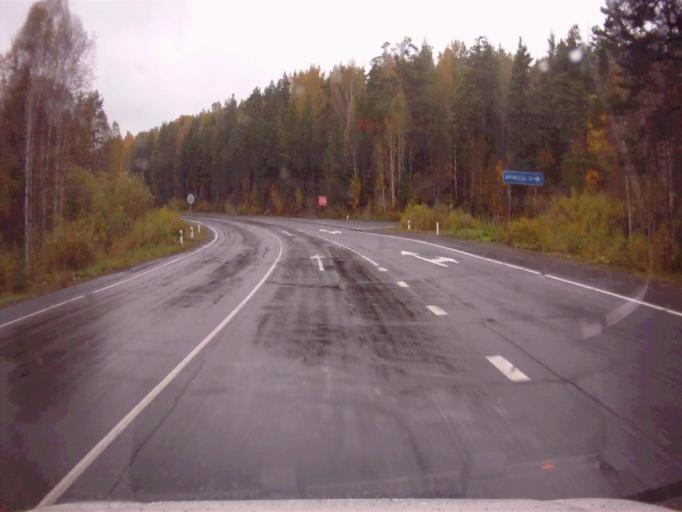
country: RU
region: Chelyabinsk
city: Verkhniy Ufaley
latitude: 55.9658
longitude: 60.3822
